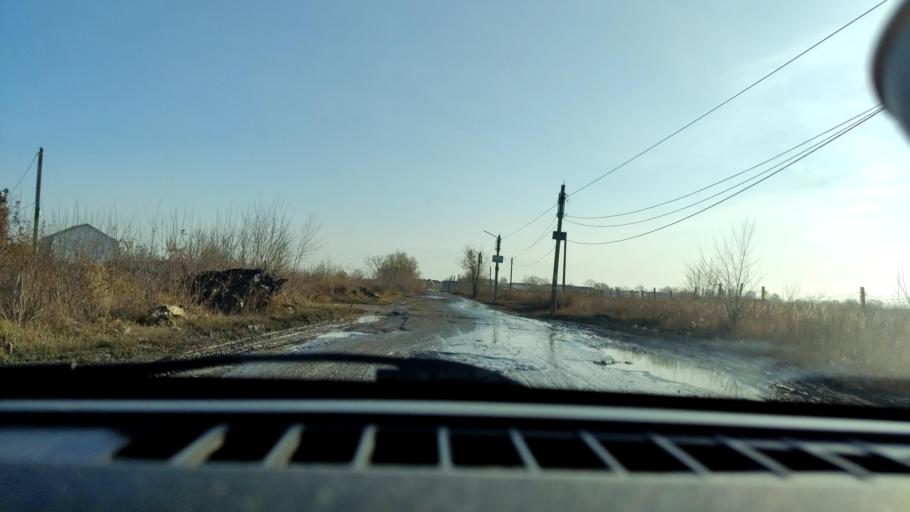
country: RU
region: Samara
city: Samara
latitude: 53.1188
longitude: 50.1057
